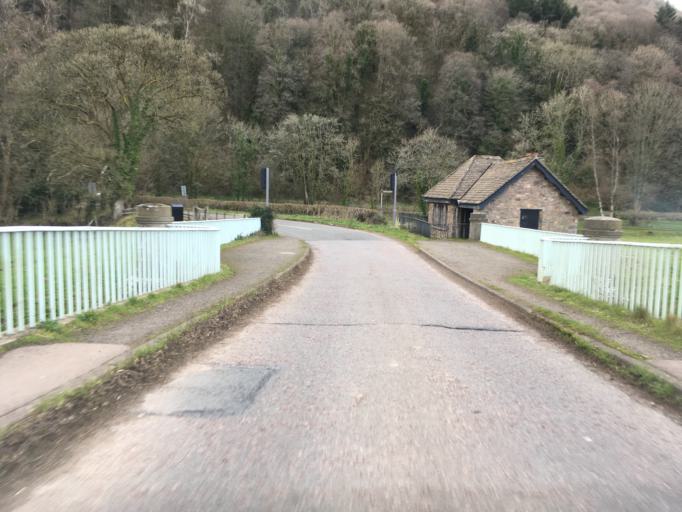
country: GB
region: Wales
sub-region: Monmouthshire
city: Tintern
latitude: 51.7428
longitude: -2.6699
